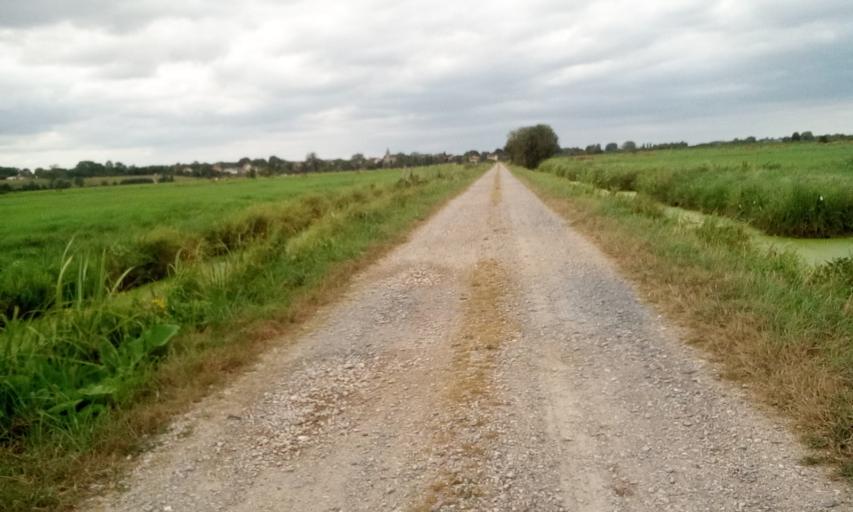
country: FR
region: Lower Normandy
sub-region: Departement du Calvados
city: Troarn
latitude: 49.1904
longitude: -0.1674
